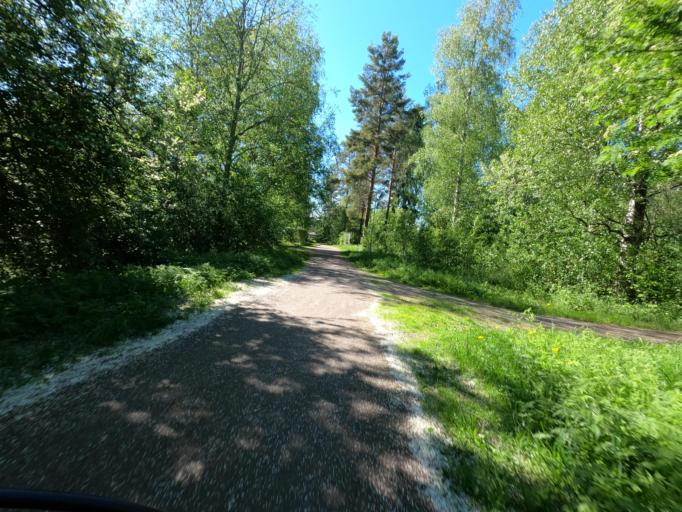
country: FI
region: North Karelia
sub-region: Joensuu
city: Joensuu
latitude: 62.5958
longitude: 29.8099
